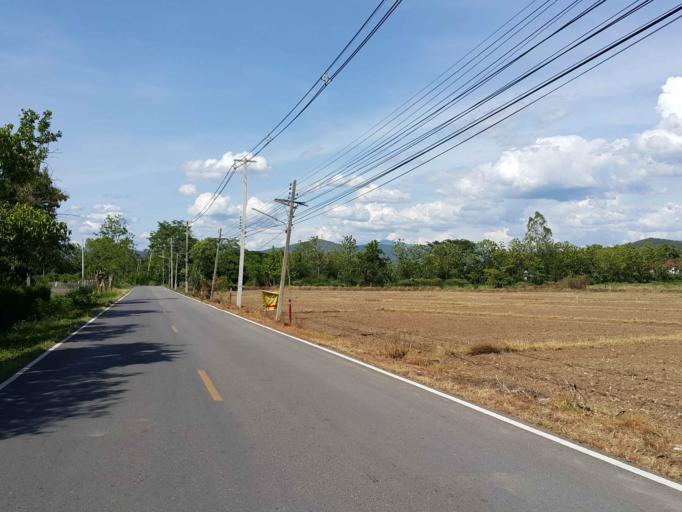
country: TH
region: Chiang Mai
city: San Kamphaeng
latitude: 18.7688
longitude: 99.1501
